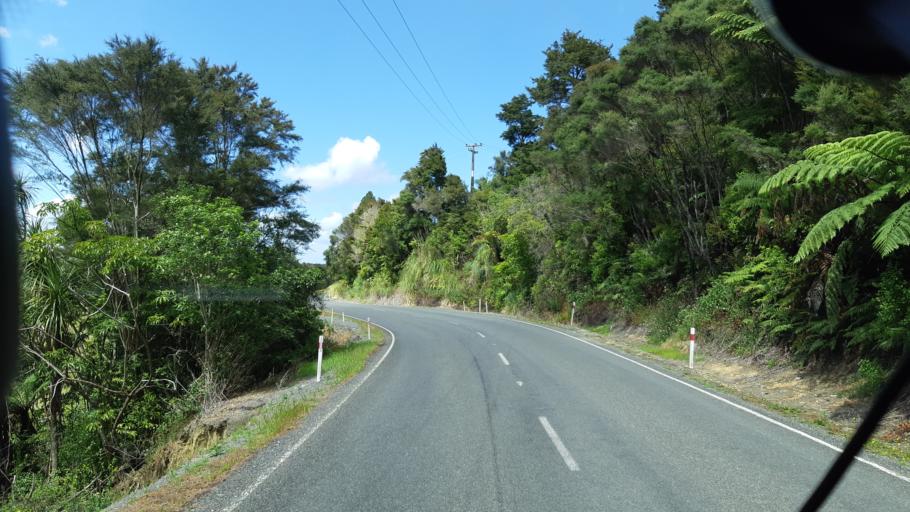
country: NZ
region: Northland
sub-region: Far North District
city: Taipa
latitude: -35.2551
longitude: 173.5348
